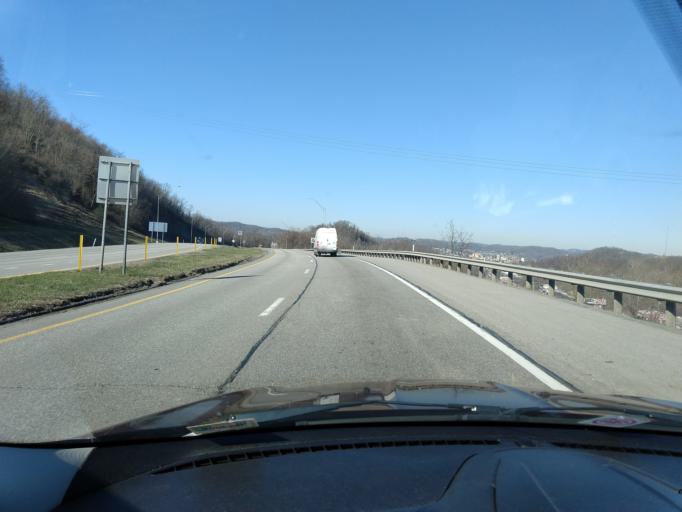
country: US
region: West Virginia
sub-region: Harrison County
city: Despard
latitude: 39.2780
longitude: -80.2946
